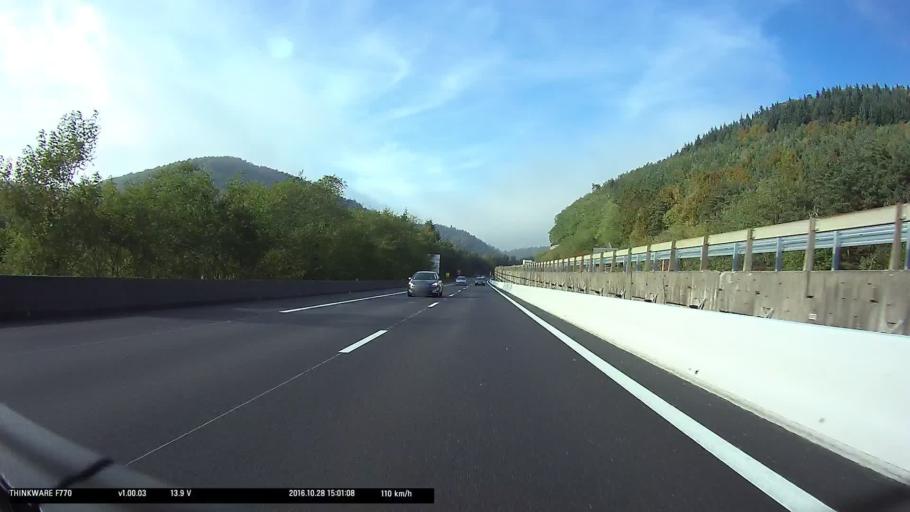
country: FR
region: Alsace
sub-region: Departement du Bas-Rhin
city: Saverne
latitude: 48.7629
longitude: 7.3452
